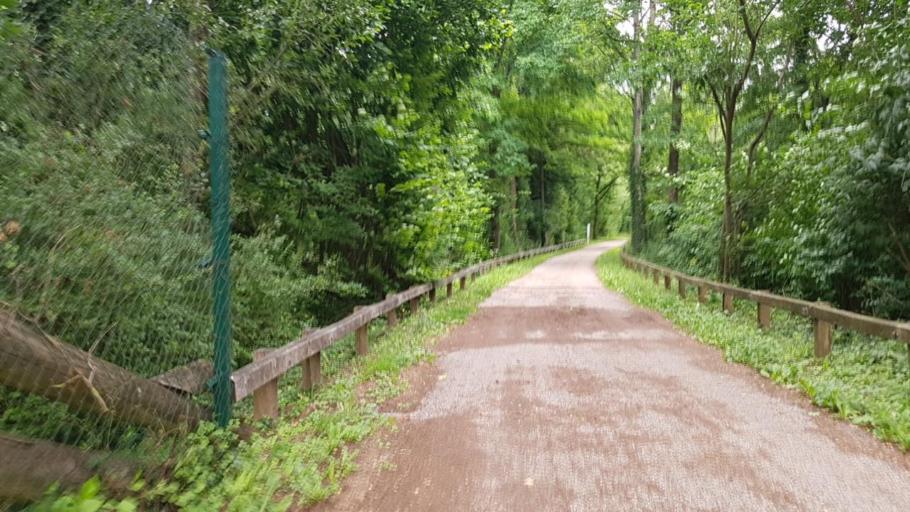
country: FR
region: Picardie
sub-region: Departement de l'Aisne
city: Origny-en-Thierache
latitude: 49.9327
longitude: 4.0196
